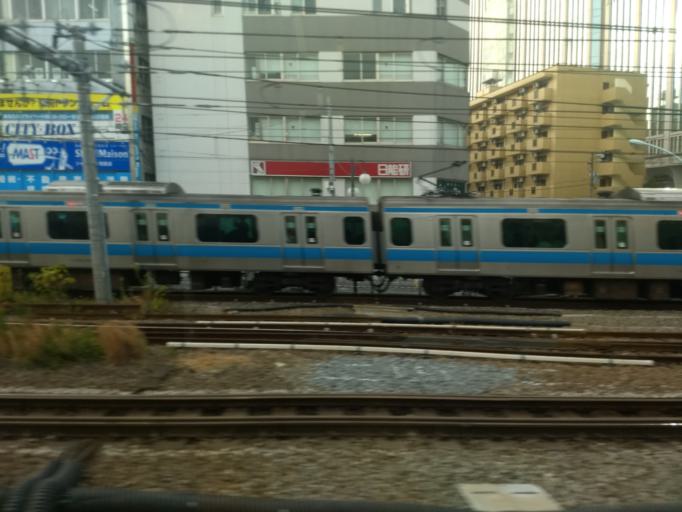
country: JP
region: Kanagawa
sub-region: Kawasaki-shi
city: Kawasaki
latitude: 35.5638
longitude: 139.7166
